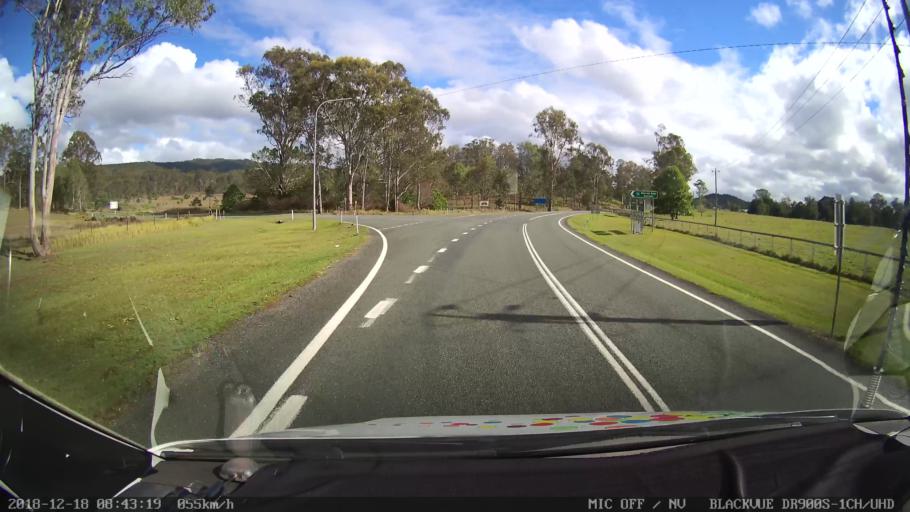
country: AU
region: Queensland
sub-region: Logan
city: Cedar Vale
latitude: -28.2193
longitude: 152.8583
